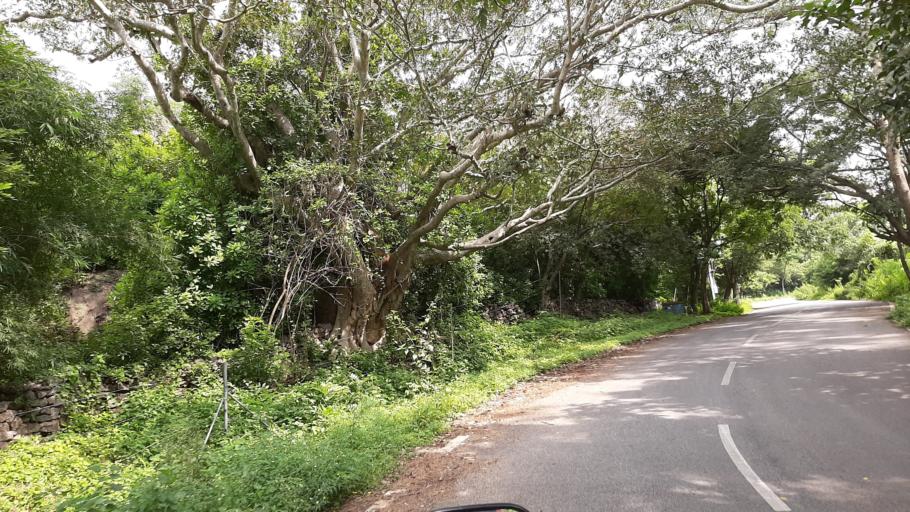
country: IN
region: Karnataka
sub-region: Ramanagara
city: Magadi
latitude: 12.9120
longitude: 77.2945
